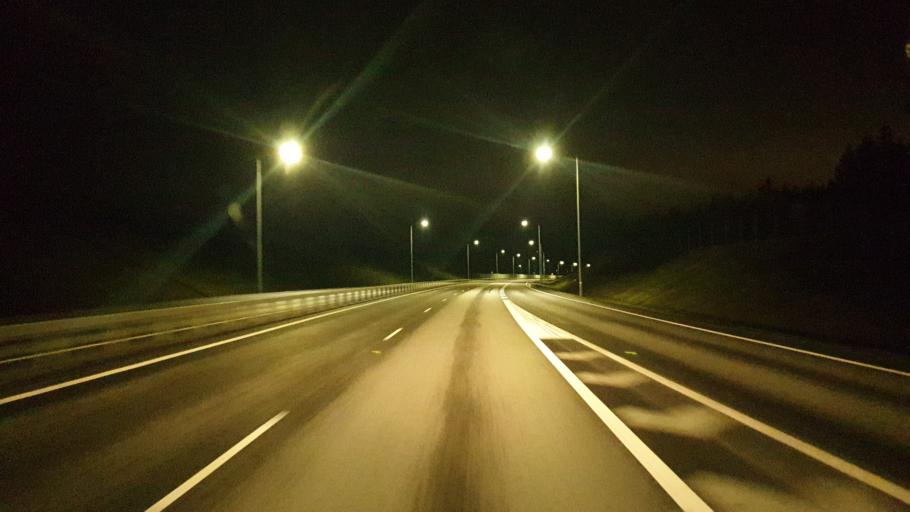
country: FI
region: Central Finland
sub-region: AEaenekoski
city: AEaenekoski
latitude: 62.5717
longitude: 25.6741
